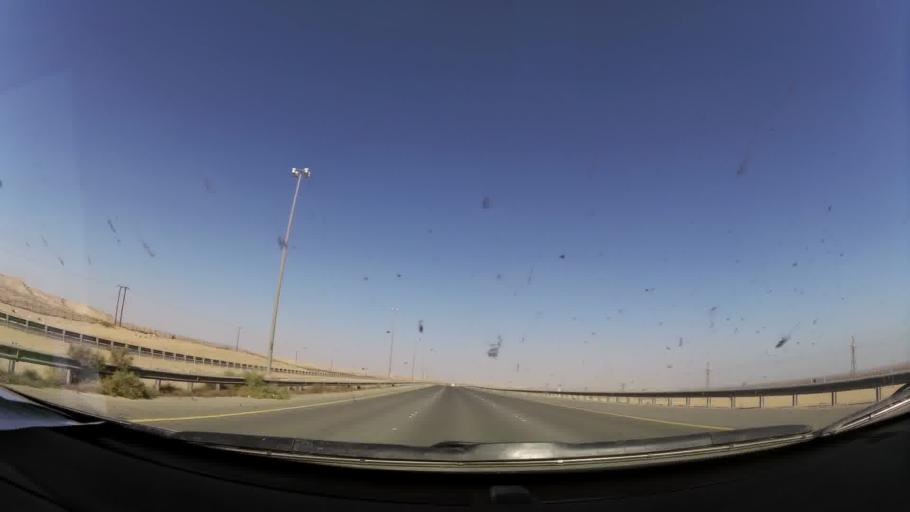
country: KW
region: Muhafazat al Jahra'
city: Al Jahra'
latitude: 29.4974
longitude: 47.7921
